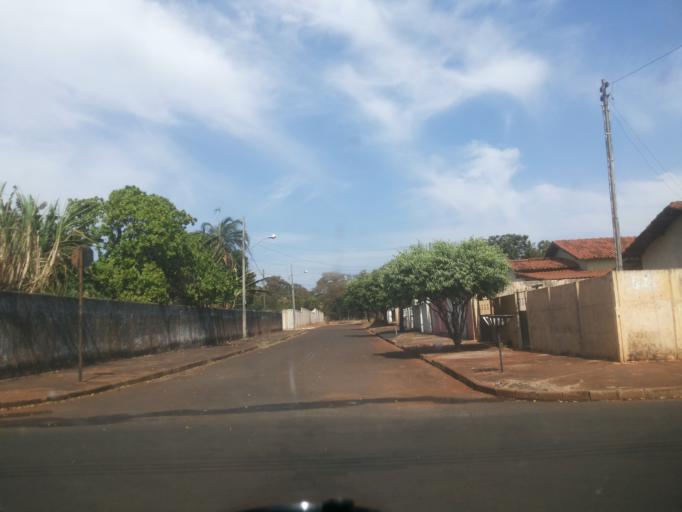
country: BR
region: Minas Gerais
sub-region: Ituiutaba
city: Ituiutaba
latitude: -18.9844
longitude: -49.4846
